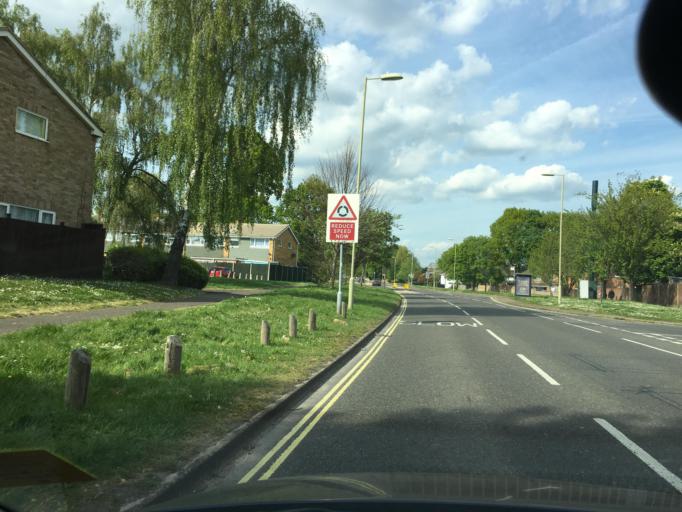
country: GB
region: England
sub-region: Hampshire
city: Farnborough
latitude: 51.3055
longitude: -0.7754
